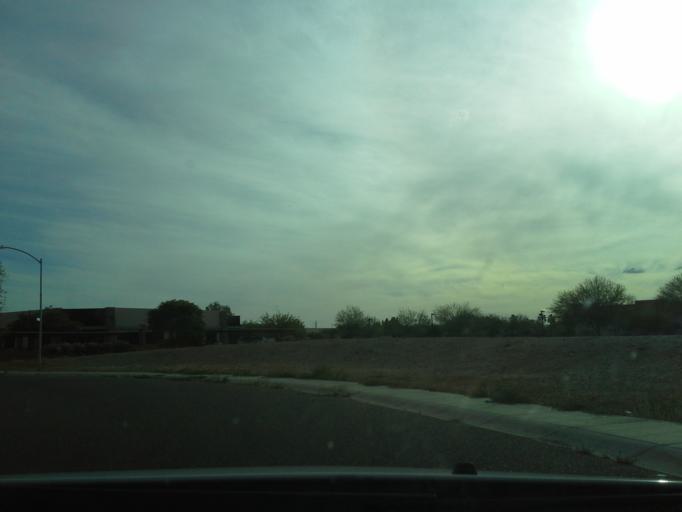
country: US
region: Arizona
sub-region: Maricopa County
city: Peoria
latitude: 33.6419
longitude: -112.2148
